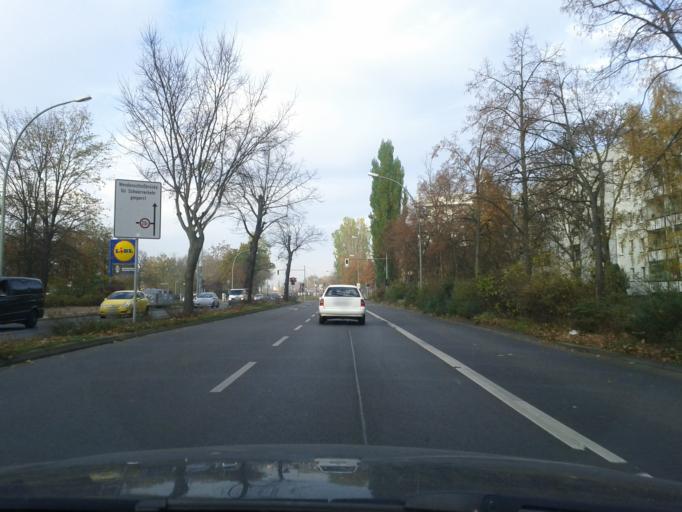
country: DE
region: Berlin
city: Berlin Koepenick
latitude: 52.4466
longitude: 13.5939
